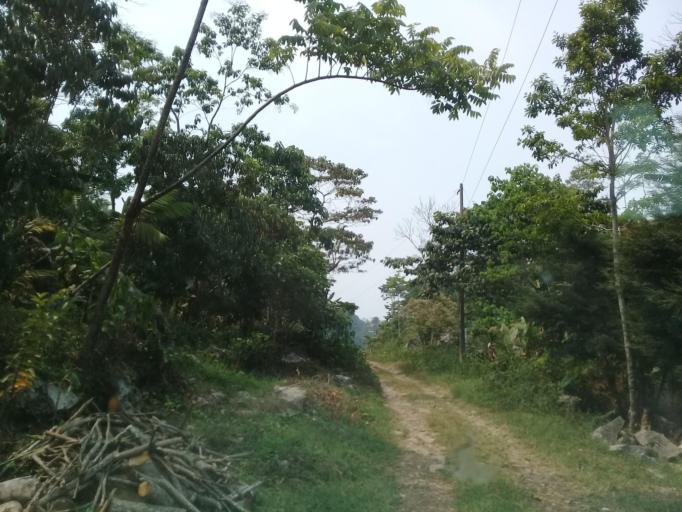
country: MX
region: Veracruz
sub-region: Tezonapa
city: Laguna Chica (Pueblo Nuevo)
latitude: 18.5873
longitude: -96.7464
